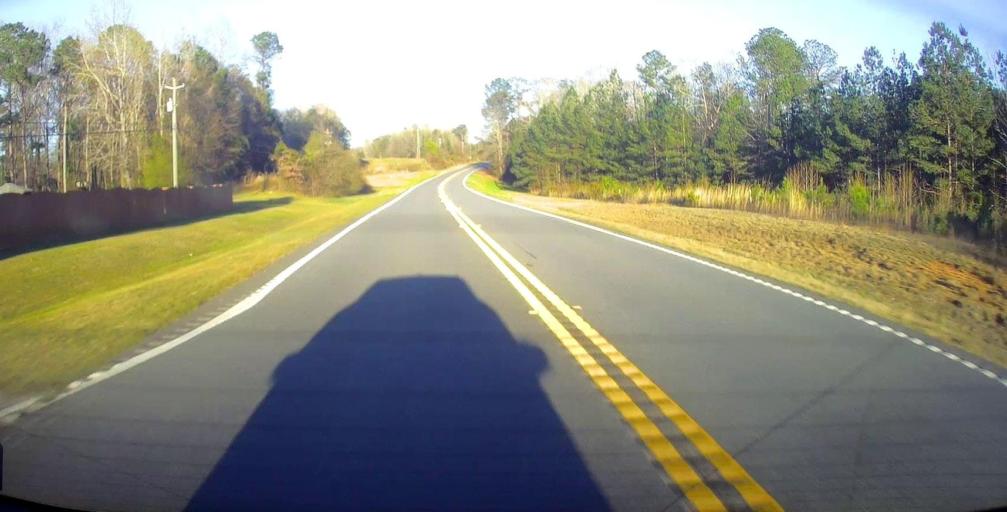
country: US
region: Georgia
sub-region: Harris County
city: Hamilton
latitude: 32.6282
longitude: -84.7785
